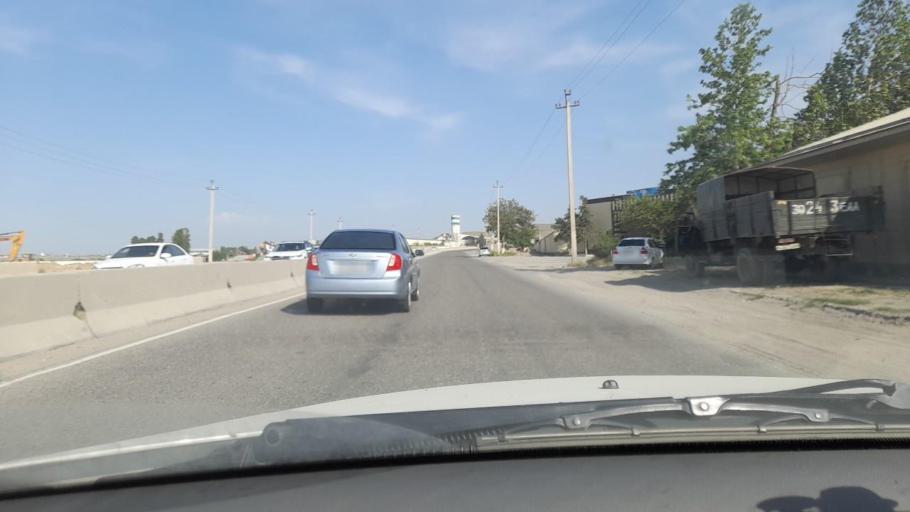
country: UZ
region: Samarqand
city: Samarqand
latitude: 39.7007
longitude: 67.0145
